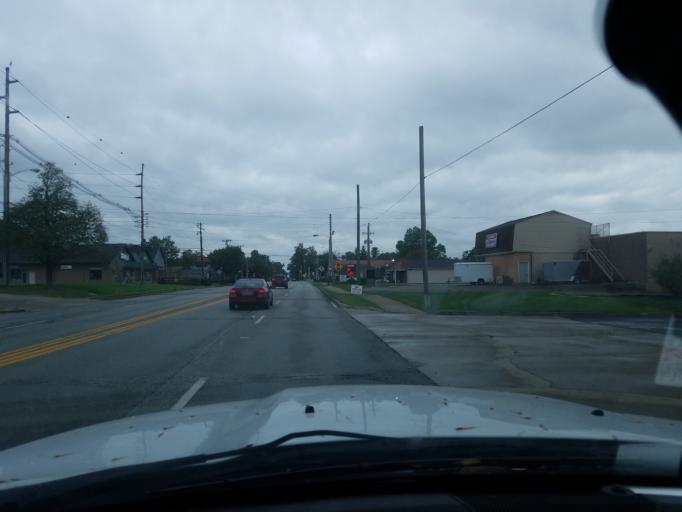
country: US
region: Kentucky
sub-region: Jefferson County
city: Lyndon
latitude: 38.2596
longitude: -85.6023
